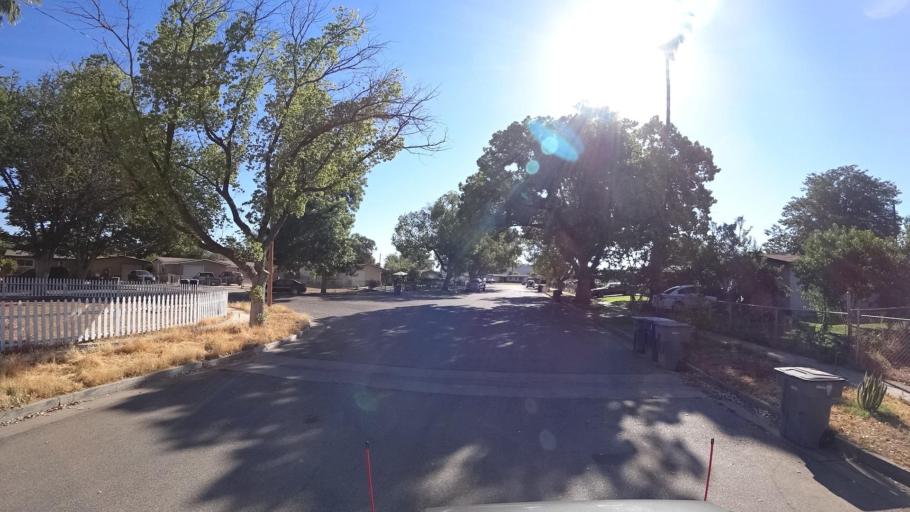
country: US
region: California
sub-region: Fresno County
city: Fresno
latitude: 36.7038
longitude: -119.7938
